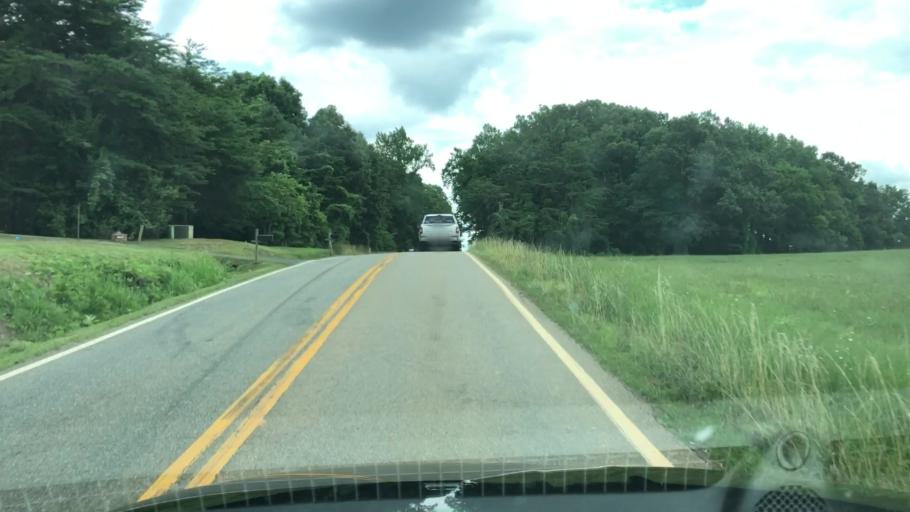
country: US
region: Virginia
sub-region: Stafford County
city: Falmouth
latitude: 38.3409
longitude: -77.5242
